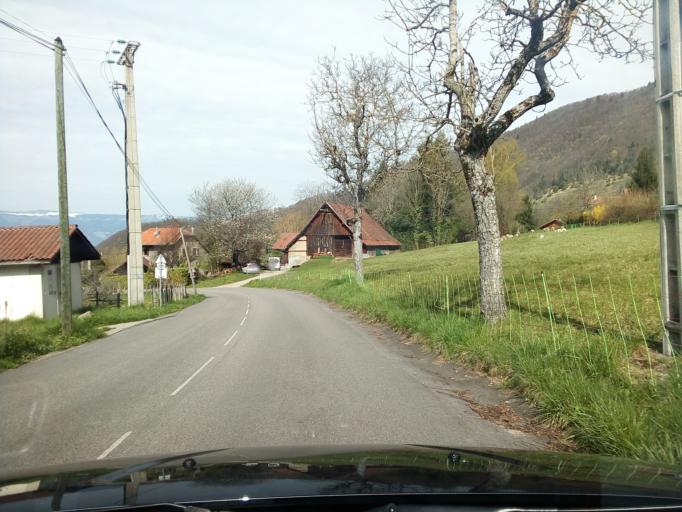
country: FR
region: Rhone-Alpes
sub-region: Departement de l'Isere
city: Revel
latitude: 45.1632
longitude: 5.8391
